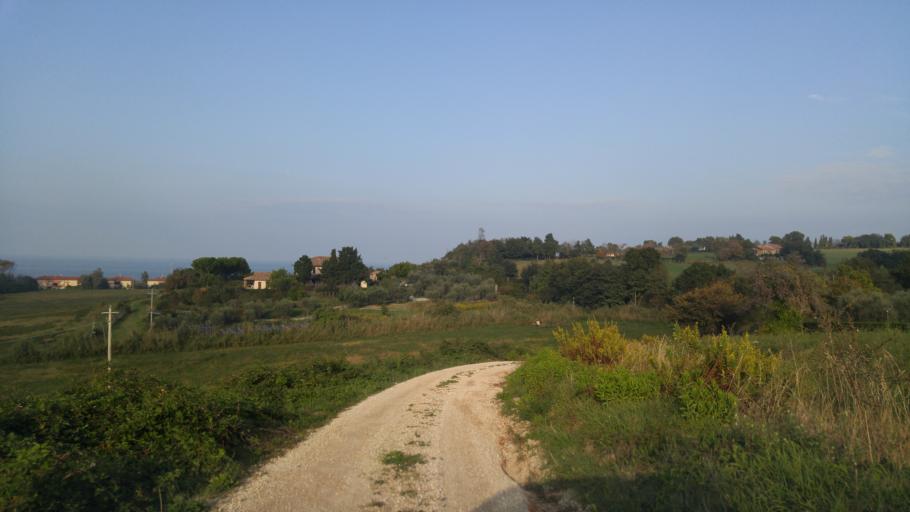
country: IT
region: The Marches
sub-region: Provincia di Pesaro e Urbino
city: Fenile
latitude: 43.8758
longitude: 12.9594
